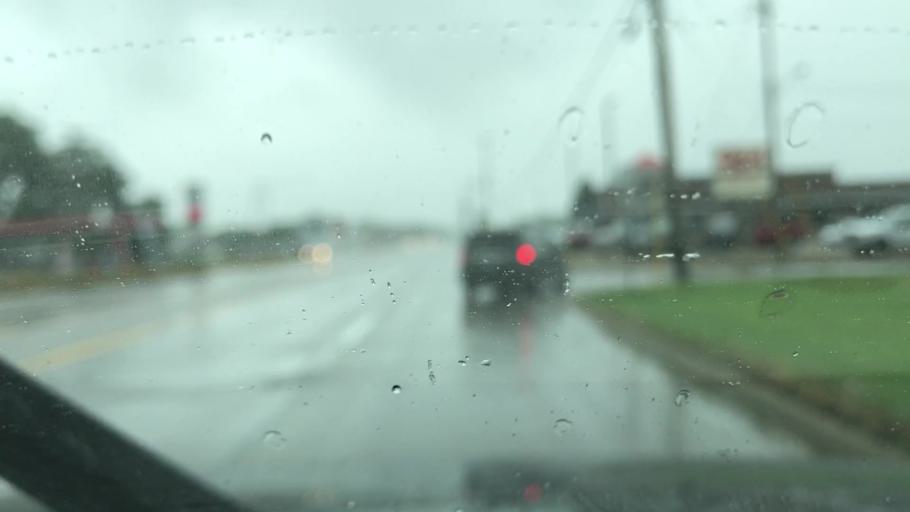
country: US
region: Michigan
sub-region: Kent County
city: Wyoming
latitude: 42.9137
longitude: -85.7320
